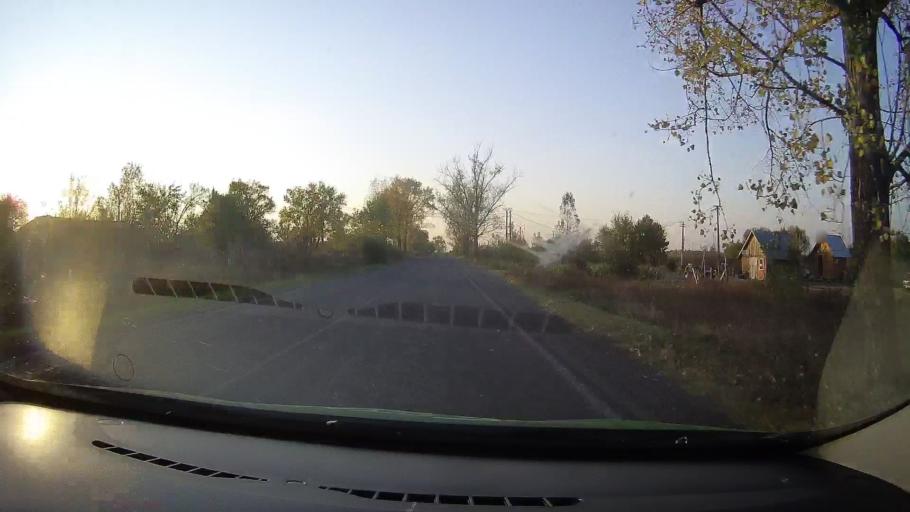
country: RO
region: Arad
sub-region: Comuna Bocsig
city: Bocsig
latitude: 46.4232
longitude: 21.9184
